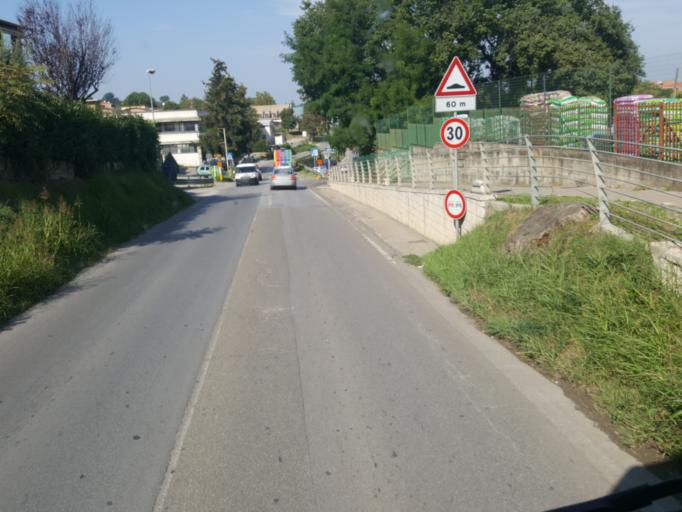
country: IT
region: Tuscany
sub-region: Provincia di Siena
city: Colle di Val d'Elsa
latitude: 43.4062
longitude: 11.1339
